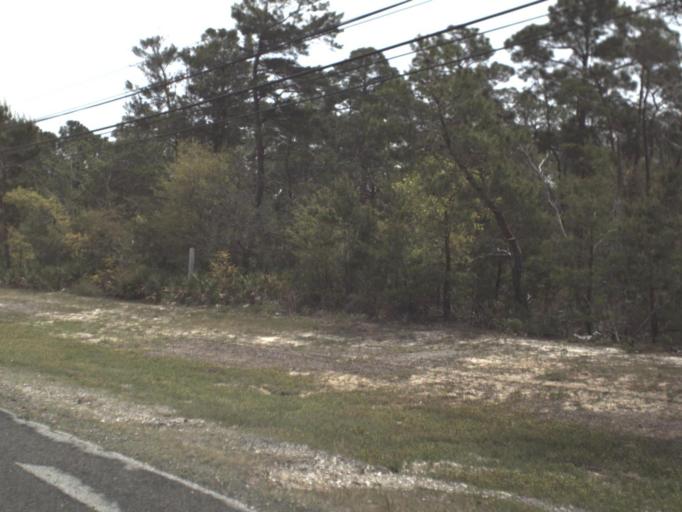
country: US
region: Florida
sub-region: Santa Rosa County
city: Holley
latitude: 30.4020
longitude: -86.9279
